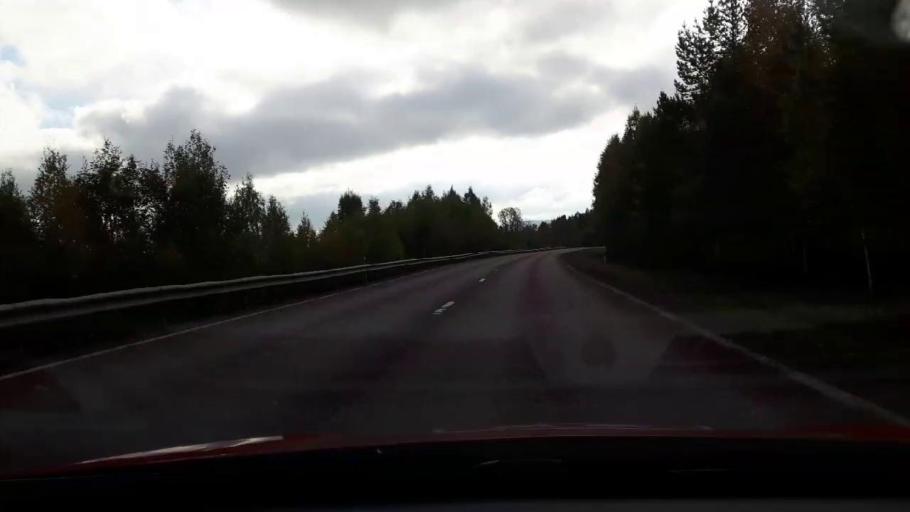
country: SE
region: Gaevleborg
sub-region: Ljusdals Kommun
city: Jaervsoe
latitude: 61.6164
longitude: 16.2943
